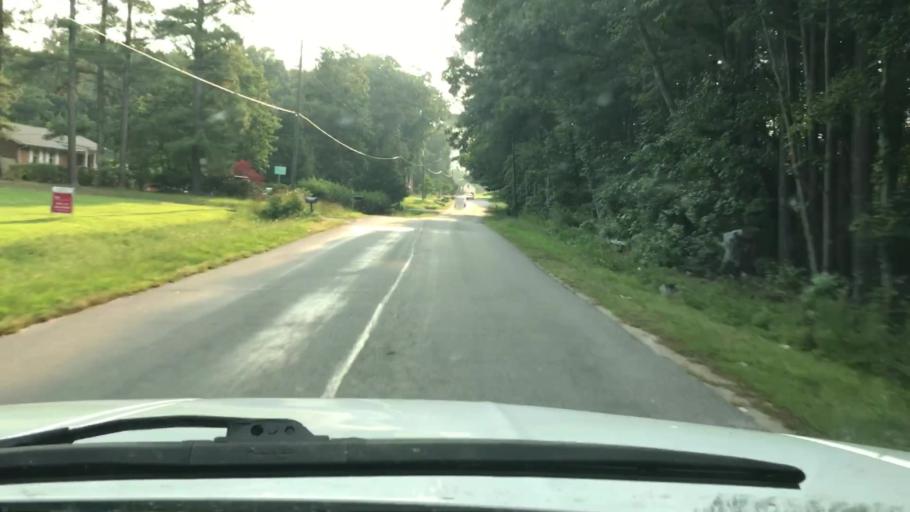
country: US
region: Virginia
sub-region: Chesterfield County
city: Chesterfield
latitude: 37.4365
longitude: -77.5212
